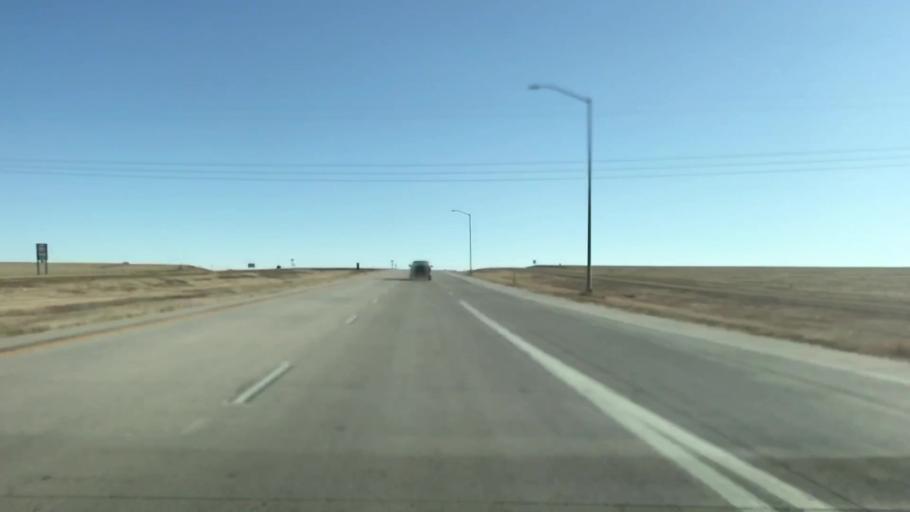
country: US
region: Colorado
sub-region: Lincoln County
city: Limon
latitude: 39.2637
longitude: -103.6408
